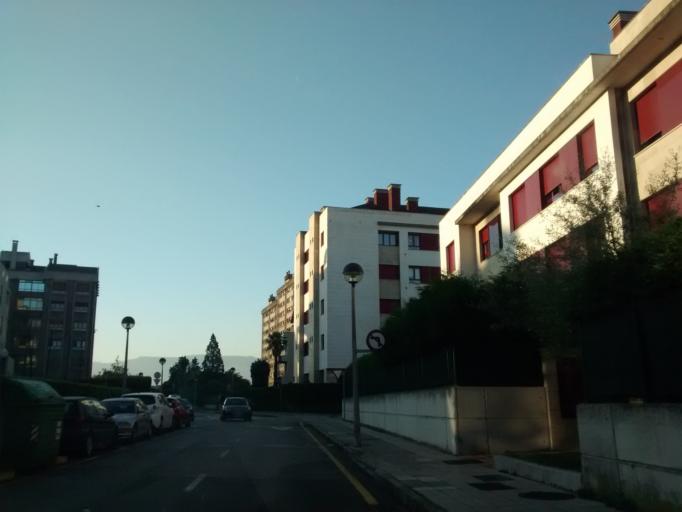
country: ES
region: Asturias
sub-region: Province of Asturias
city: Gijon
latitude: 43.5327
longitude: -5.6421
